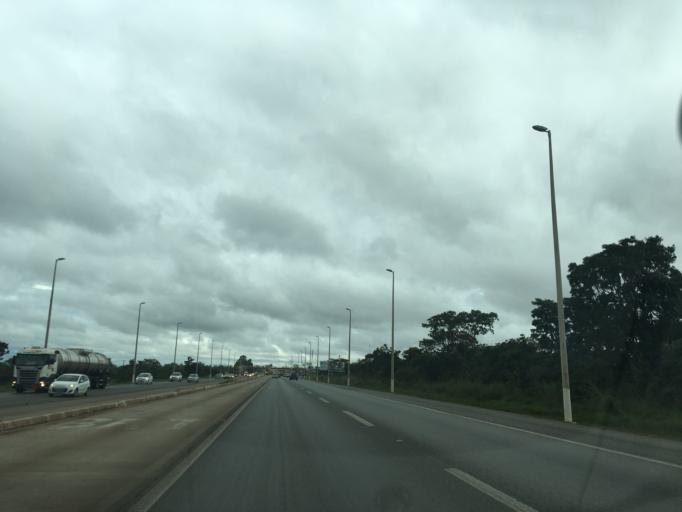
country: BR
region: Federal District
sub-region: Brasilia
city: Brasilia
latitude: -15.9866
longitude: -47.9875
